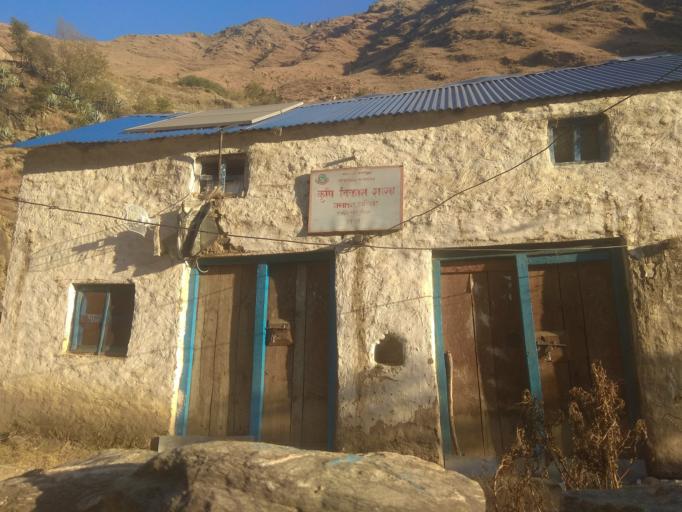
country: NP
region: Mid Western
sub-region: Bheri Zone
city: Dailekh
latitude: 29.2772
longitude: 81.7304
